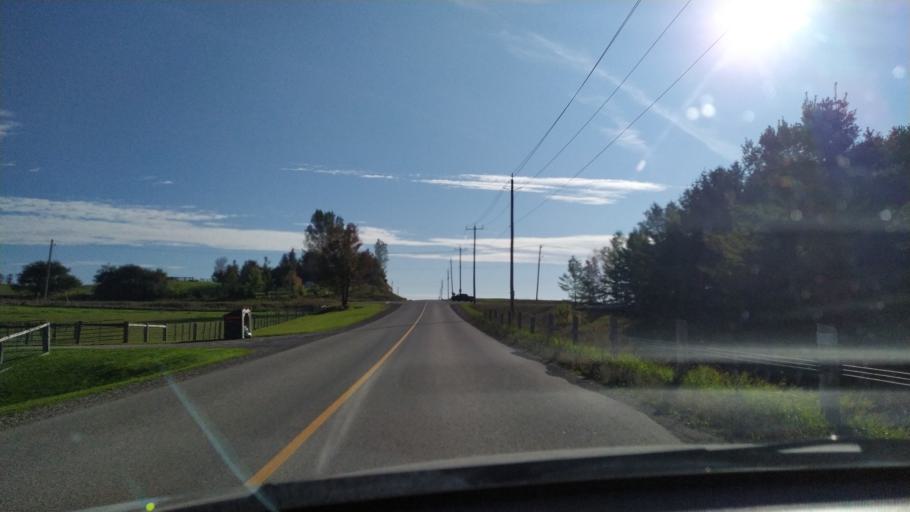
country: CA
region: Ontario
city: Waterloo
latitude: 43.4948
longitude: -80.7504
